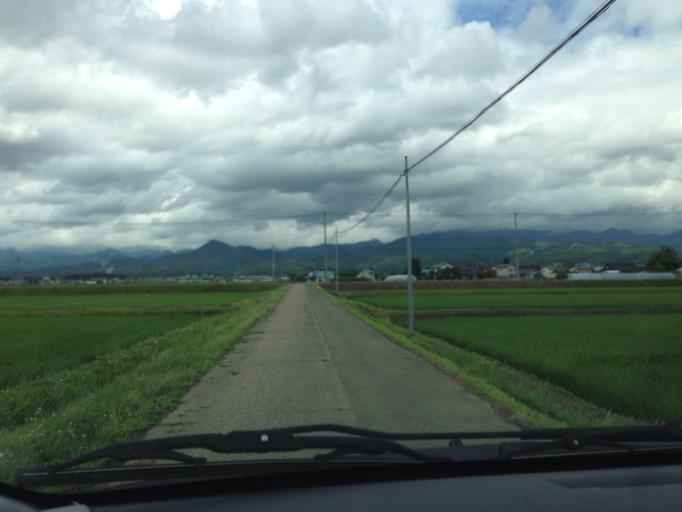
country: JP
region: Fukushima
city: Kitakata
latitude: 37.6354
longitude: 139.9040
